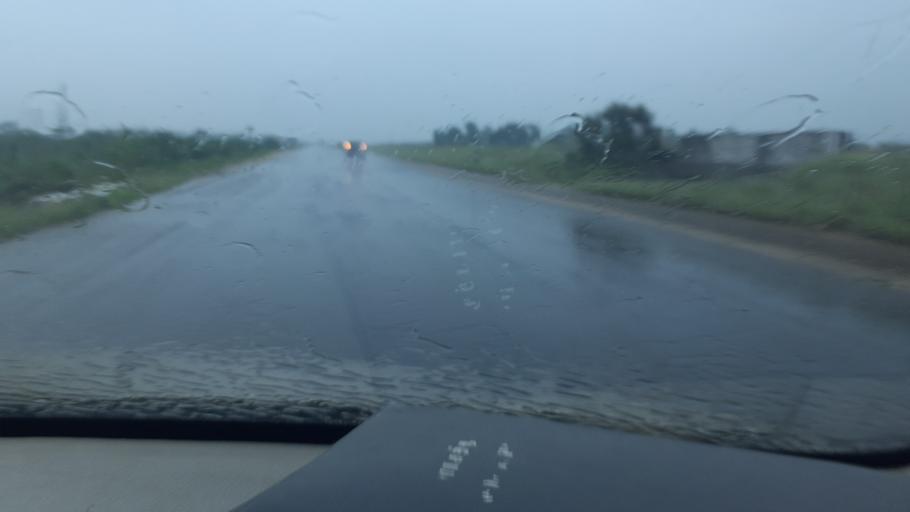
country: IN
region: Tamil Nadu
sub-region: Virudhunagar
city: Sattur
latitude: 9.4224
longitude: 77.9174
